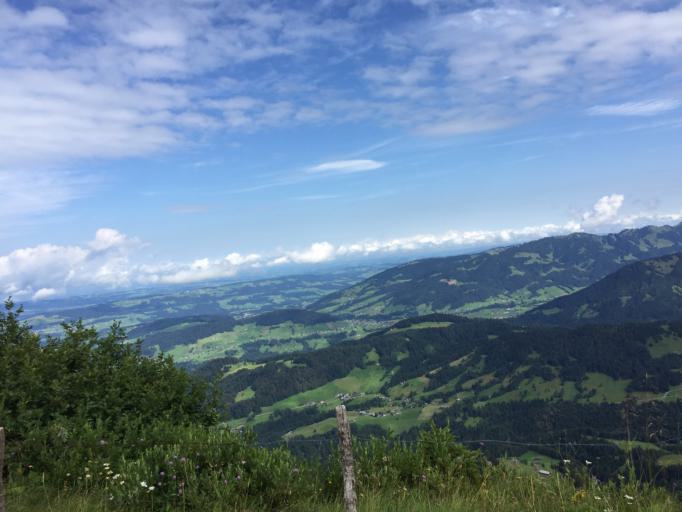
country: AT
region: Vorarlberg
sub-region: Politischer Bezirk Bregenz
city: Bizau
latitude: 47.4019
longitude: 9.9469
